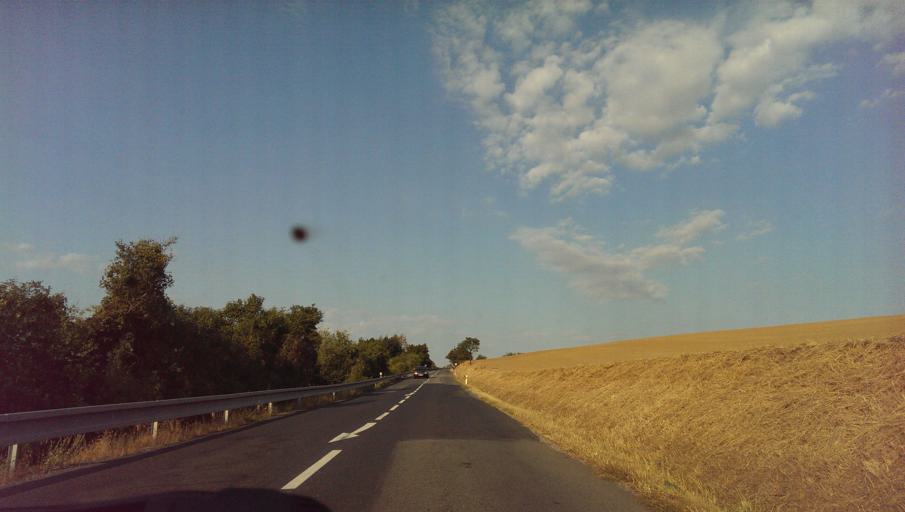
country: CZ
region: South Moravian
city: Domanin
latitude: 49.0529
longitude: 17.2804
